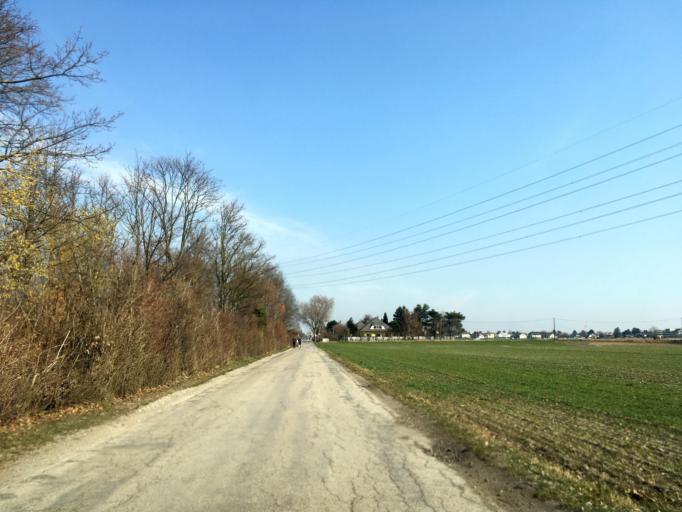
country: AT
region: Lower Austria
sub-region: Politischer Bezirk Ganserndorf
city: Gross-Enzersdorf
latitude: 48.2014
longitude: 16.4958
